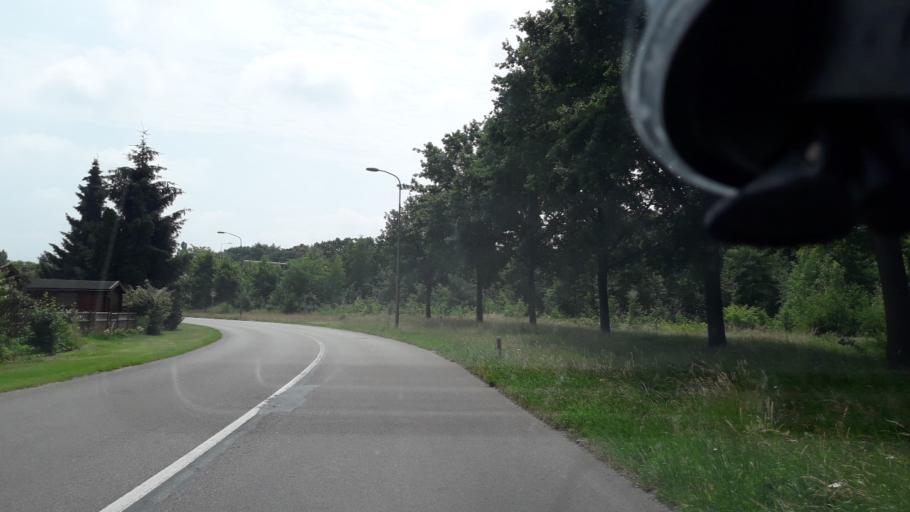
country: NL
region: Gelderland
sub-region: Gemeente Harderwijk
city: Harderwijk
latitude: 52.3514
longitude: 5.6389
